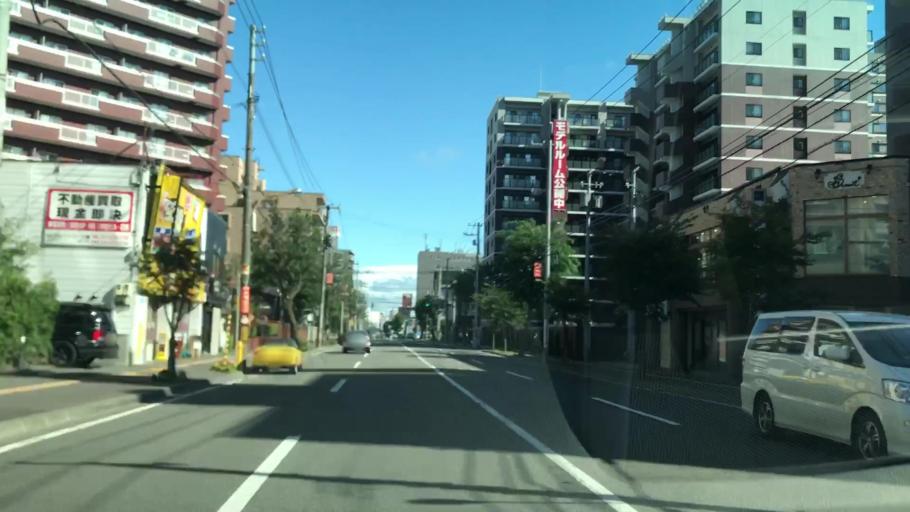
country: JP
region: Hokkaido
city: Sapporo
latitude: 43.0791
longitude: 141.3077
